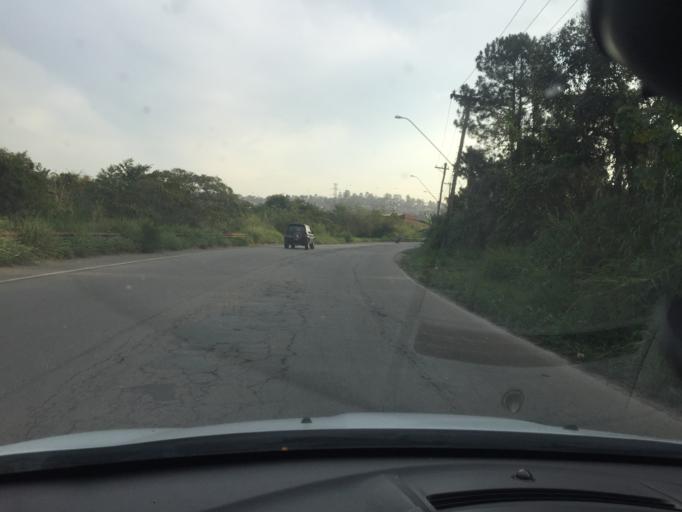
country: BR
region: Sao Paulo
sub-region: Campo Limpo Paulista
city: Campo Limpo Paulista
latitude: -23.2072
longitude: -46.8050
